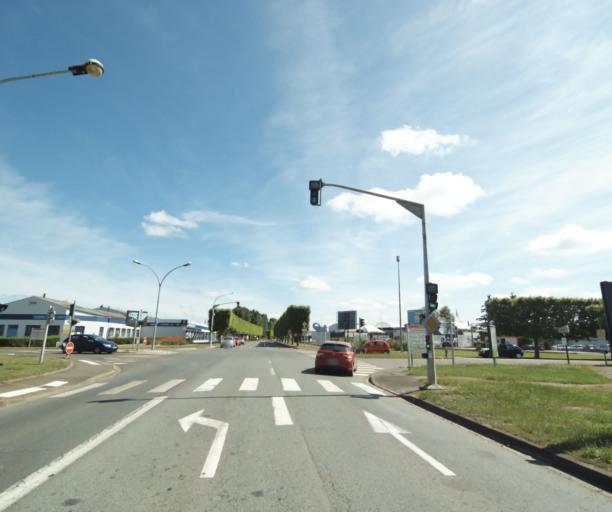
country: FR
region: Centre
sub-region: Departement d'Eure-et-Loir
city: Luce
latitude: 48.4307
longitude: 1.4635
